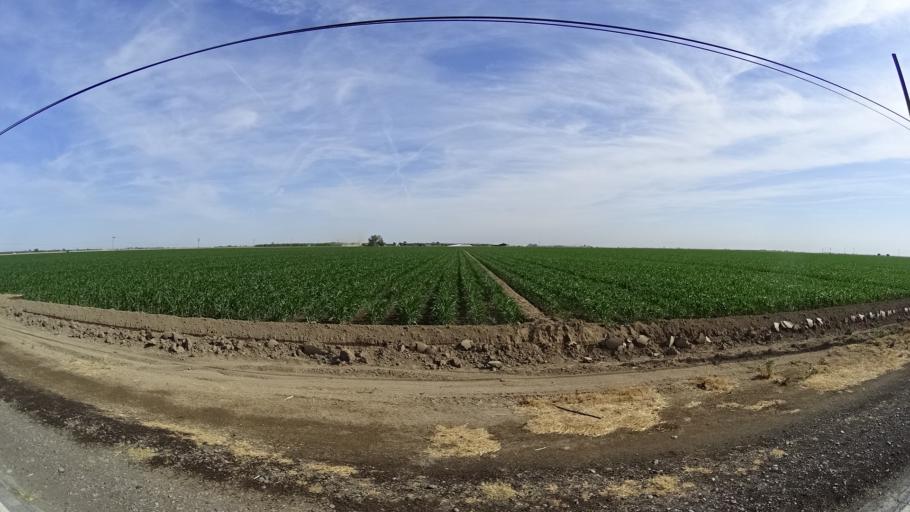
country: US
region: California
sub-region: Kings County
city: Home Garden
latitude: 36.3429
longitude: -119.5446
